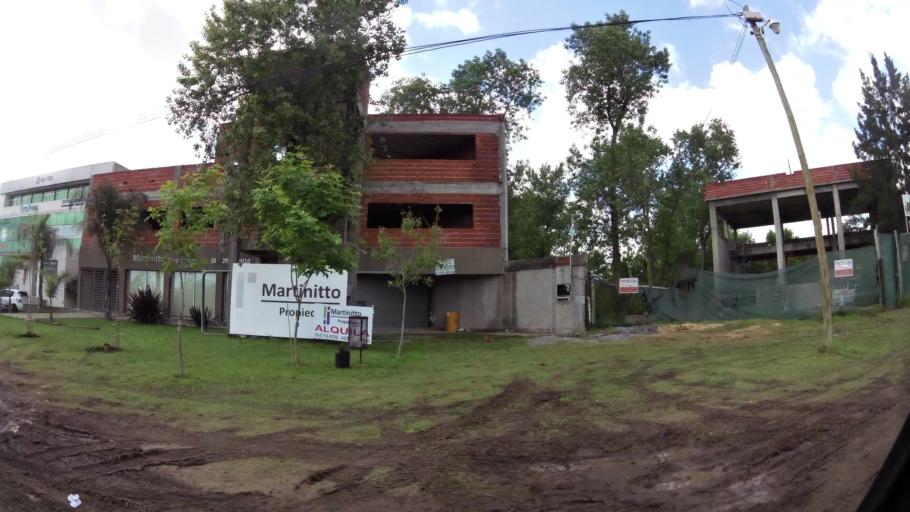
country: AR
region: Buenos Aires
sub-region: Partido de Quilmes
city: Quilmes
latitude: -34.8129
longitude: -58.1780
